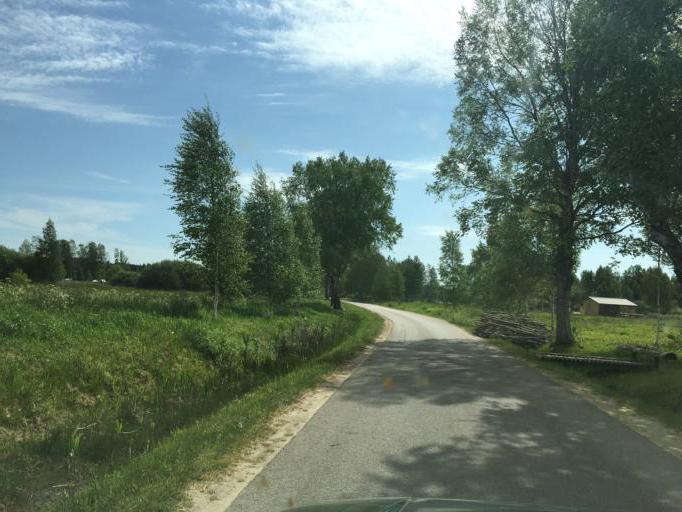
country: LV
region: Talsu Rajons
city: Valdemarpils
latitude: 57.3671
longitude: 22.6016
